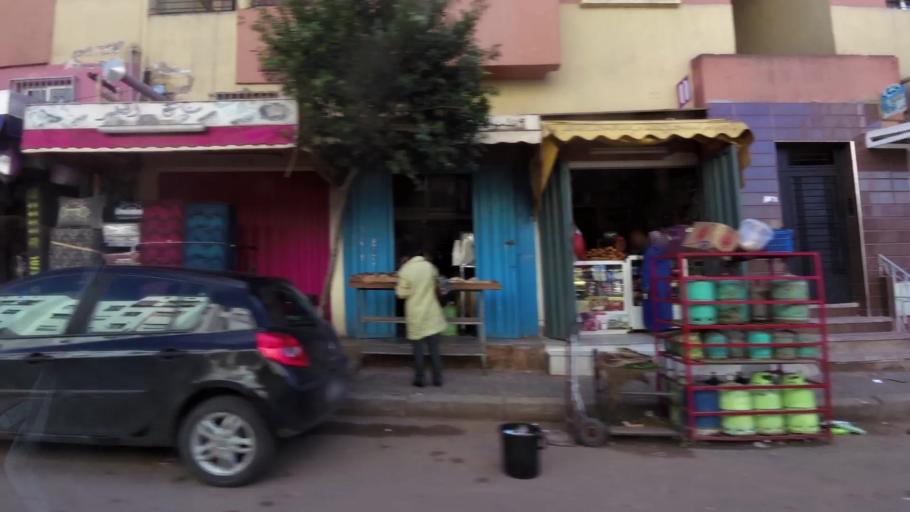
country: MA
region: Grand Casablanca
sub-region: Casablanca
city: Casablanca
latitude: 33.5484
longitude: -7.7035
